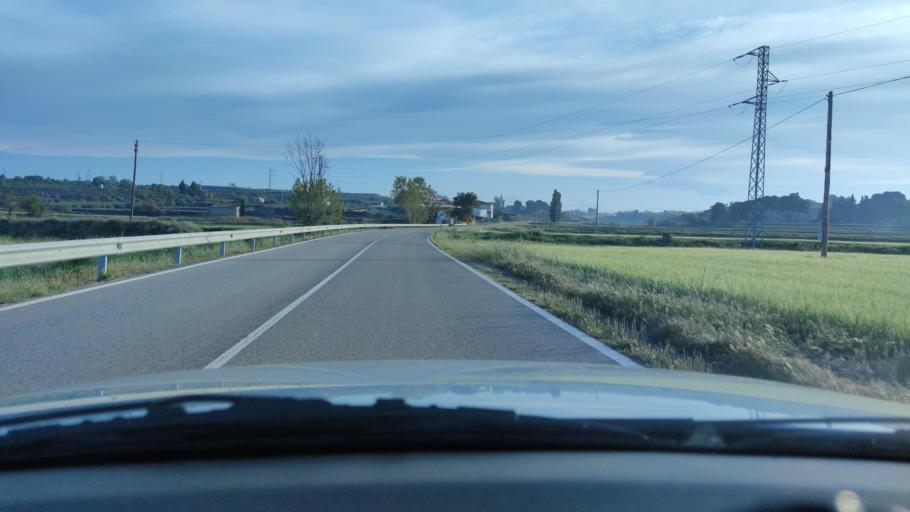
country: ES
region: Catalonia
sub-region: Provincia de Lleida
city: Castellsera
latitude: 41.7560
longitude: 0.9949
